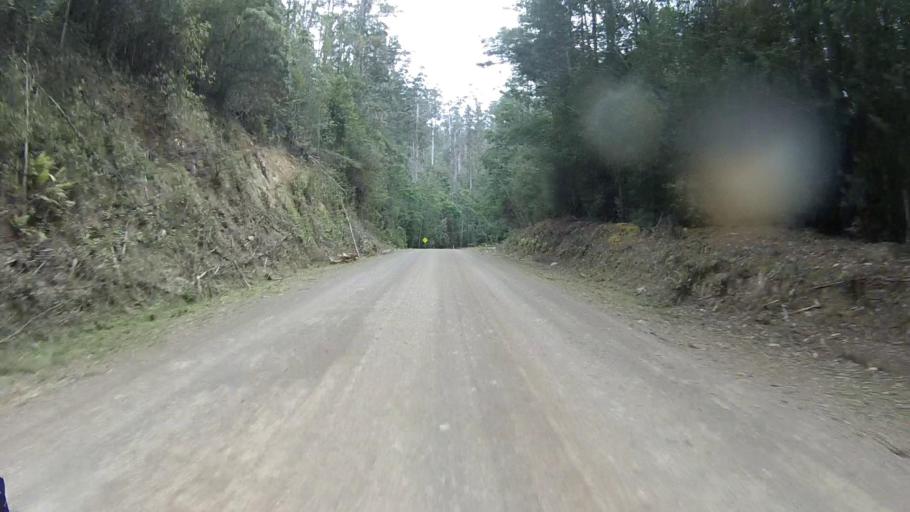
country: AU
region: Tasmania
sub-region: Sorell
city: Sorell
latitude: -42.7074
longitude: 147.8434
